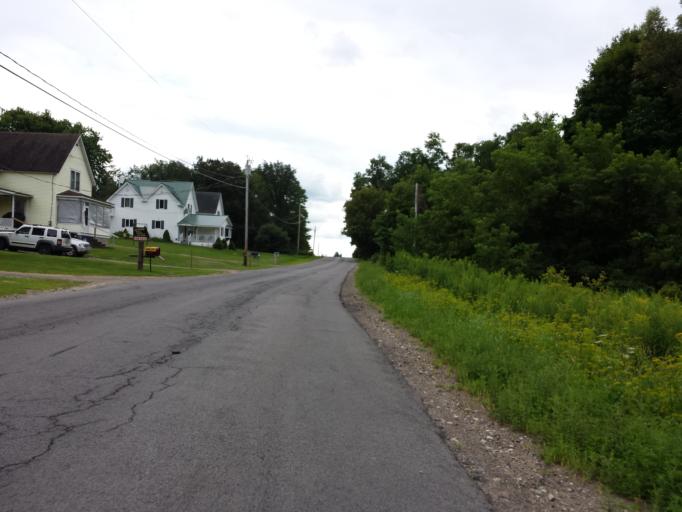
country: US
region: New York
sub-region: St. Lawrence County
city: Norwood
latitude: 44.7087
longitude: -74.9998
